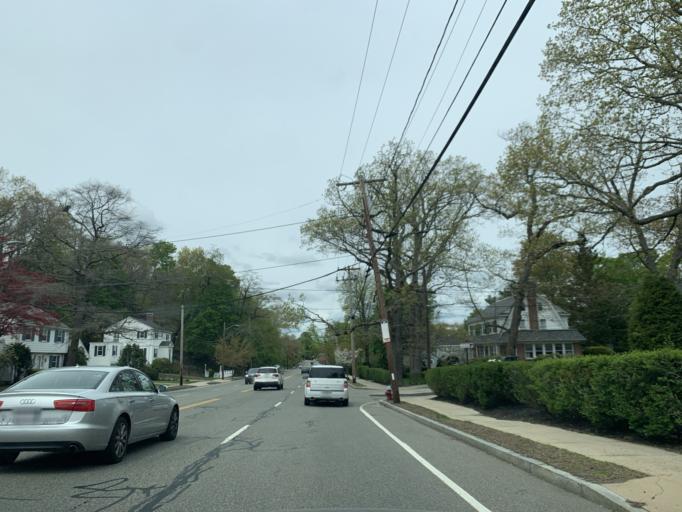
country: US
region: Massachusetts
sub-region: Norfolk County
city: Milton
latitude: 42.2507
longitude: -71.0733
